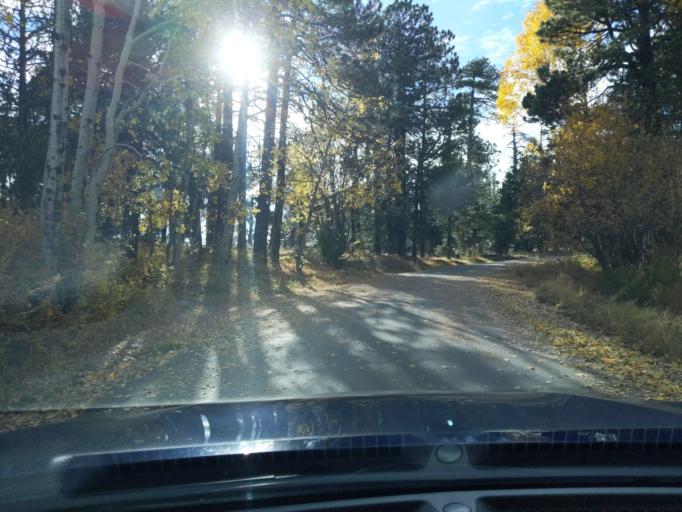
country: US
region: Arizona
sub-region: Pima County
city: Catalina
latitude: 32.4404
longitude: -110.7864
